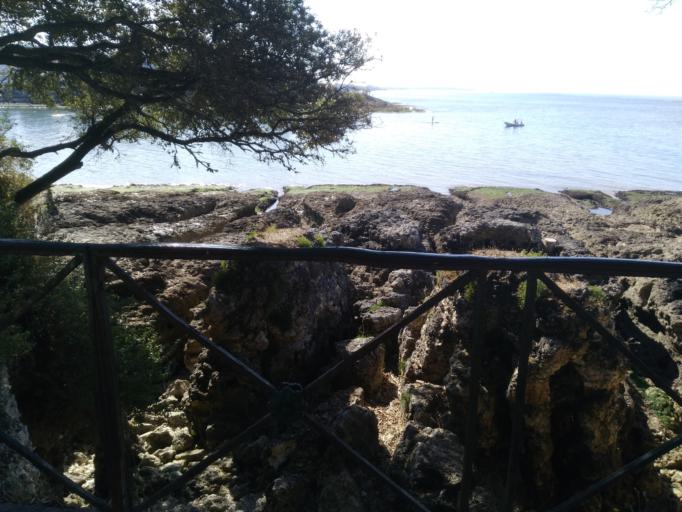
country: FR
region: Poitou-Charentes
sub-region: Departement de la Charente-Maritime
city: Saint-Palais-sur-Mer
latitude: 45.6401
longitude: -1.0909
